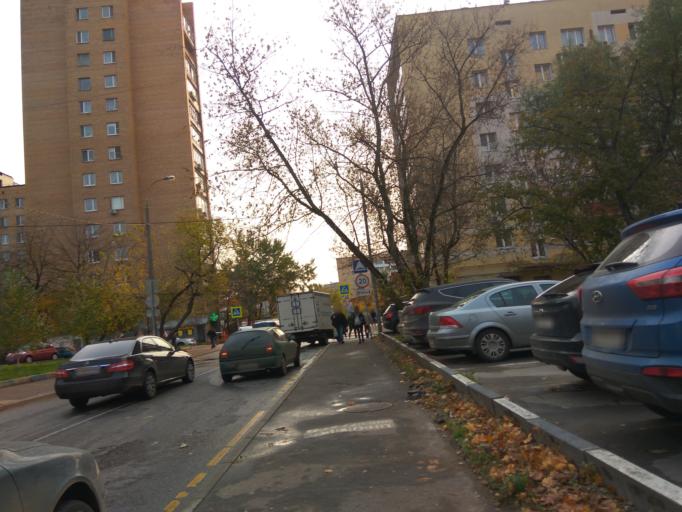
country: RU
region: Moskovskaya
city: Bogorodskoye
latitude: 55.7979
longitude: 37.7179
